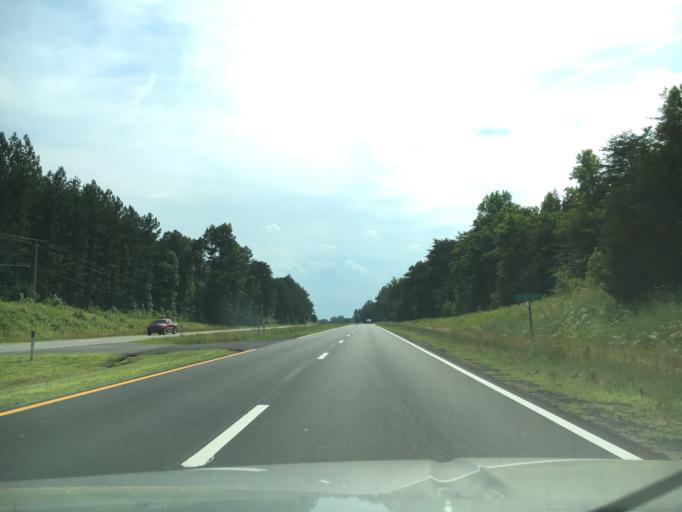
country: US
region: Virginia
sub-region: Halifax County
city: Halifax
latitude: 36.8171
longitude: -78.7382
